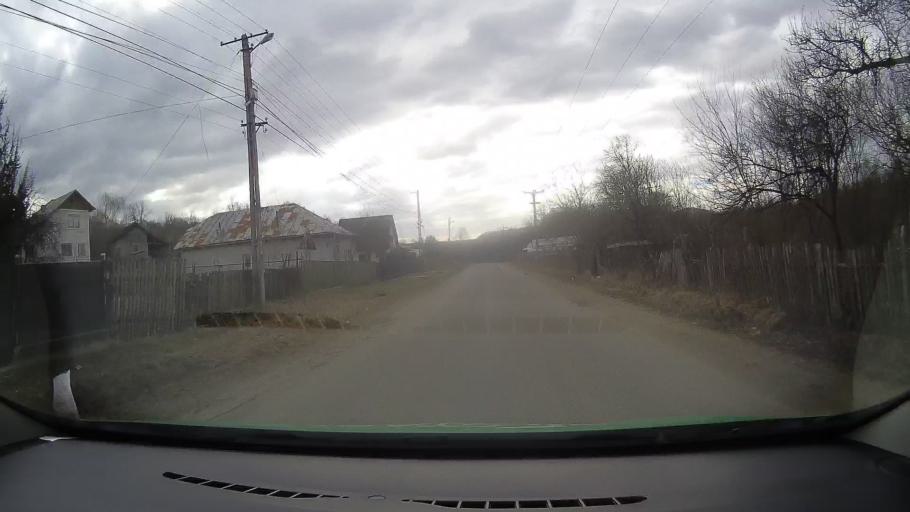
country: RO
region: Dambovita
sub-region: Comuna Valea Lunga
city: Valea Lunga-Cricov
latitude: 45.0747
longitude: 25.5768
